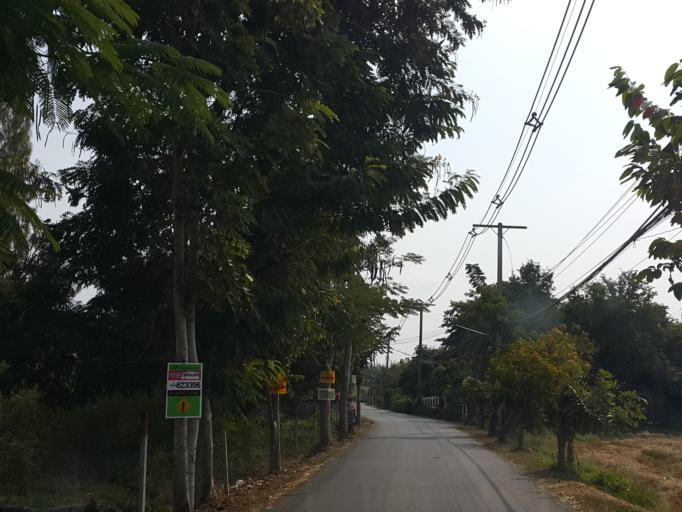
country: TH
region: Chiang Mai
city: San Kamphaeng
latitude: 18.8093
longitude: 99.1243
